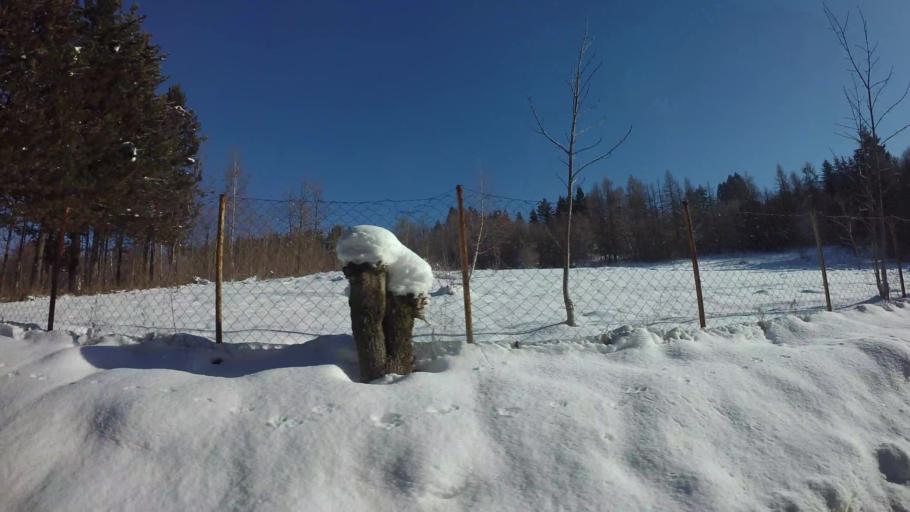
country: BA
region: Federation of Bosnia and Herzegovina
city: Kobilja Glava
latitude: 43.8872
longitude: 18.4091
